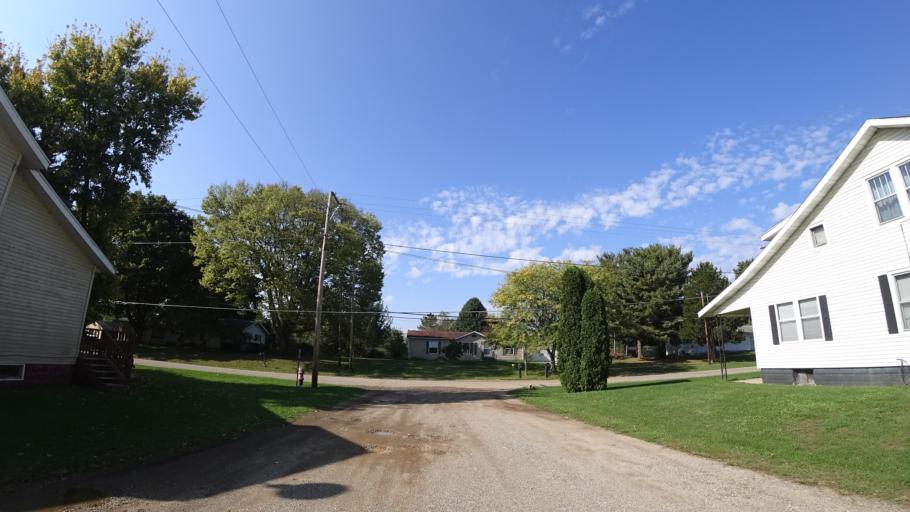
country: US
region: Michigan
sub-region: Saint Joseph County
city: Three Rivers
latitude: 41.9312
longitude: -85.6372
